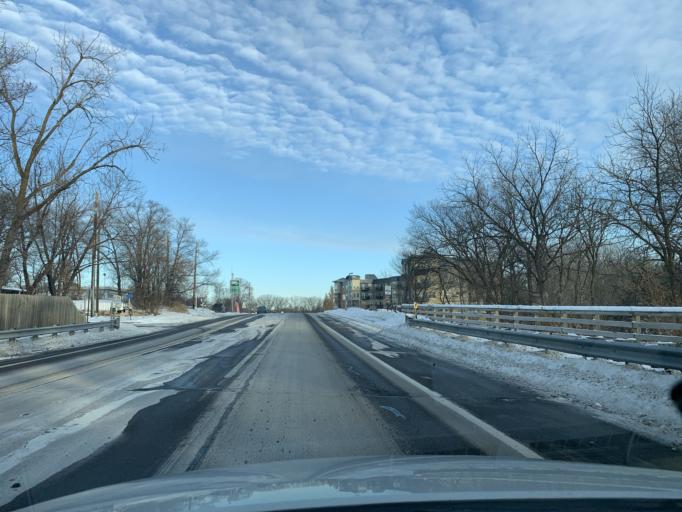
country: US
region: Minnesota
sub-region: Hennepin County
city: Minnetonka Mills
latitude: 44.9450
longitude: -93.4048
